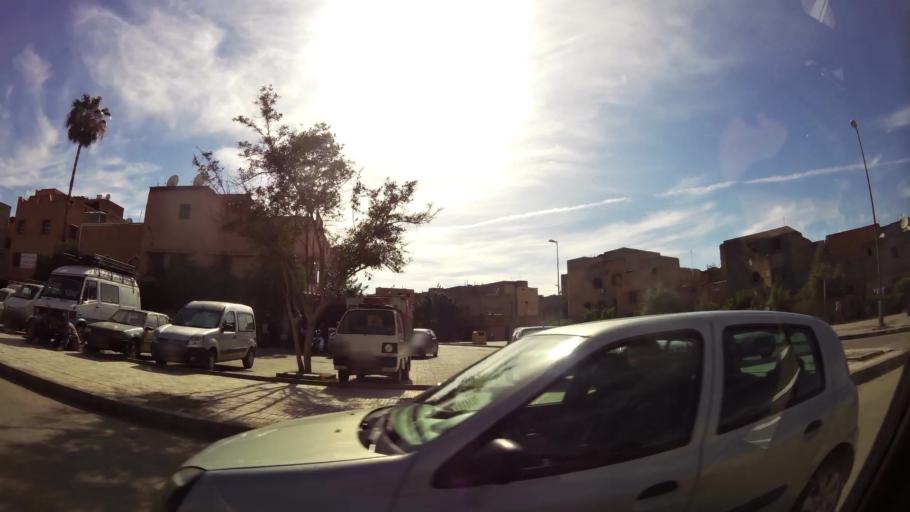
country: MA
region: Marrakech-Tensift-Al Haouz
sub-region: Marrakech
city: Marrakesh
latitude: 31.6105
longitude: -7.9575
